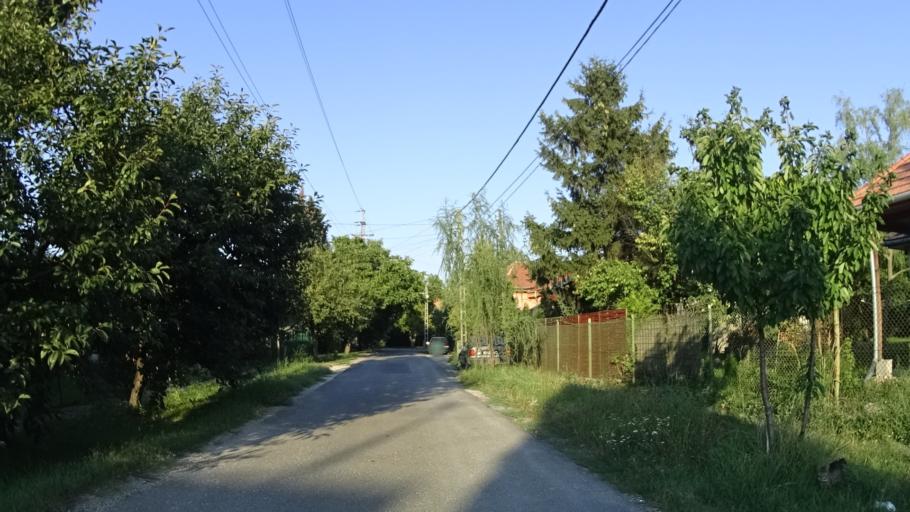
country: HU
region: Pest
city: Diosd
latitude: 47.3832
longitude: 18.9476
